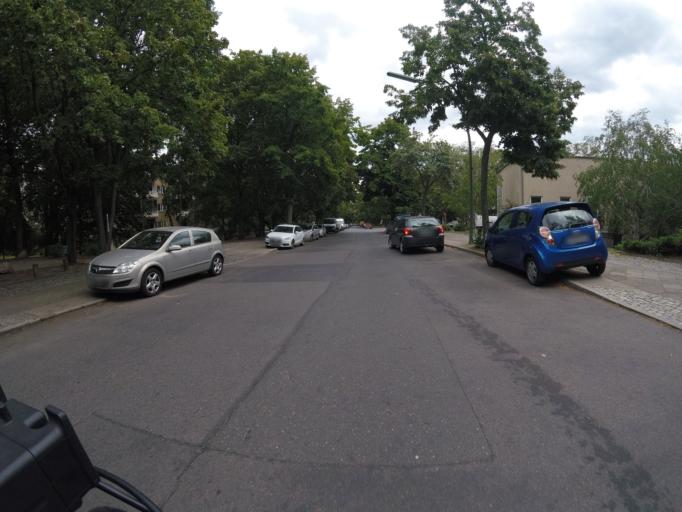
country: DE
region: Berlin
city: Charlottenburg-Nord
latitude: 52.5352
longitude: 13.2819
